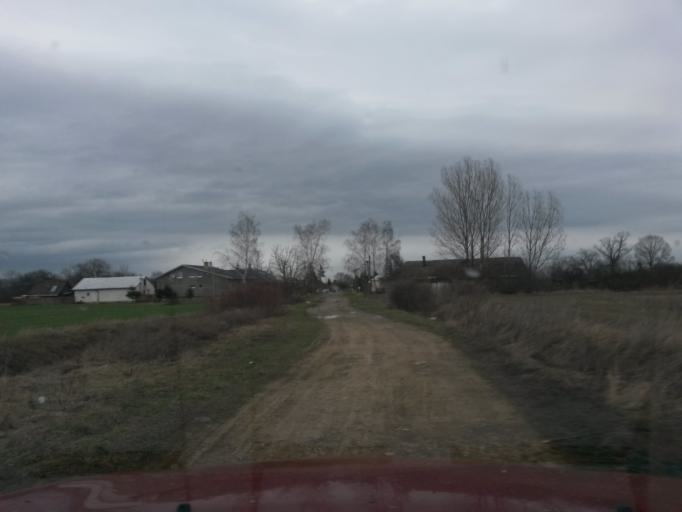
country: SK
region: Kosicky
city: Michalovce
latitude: 48.6989
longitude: 21.9107
